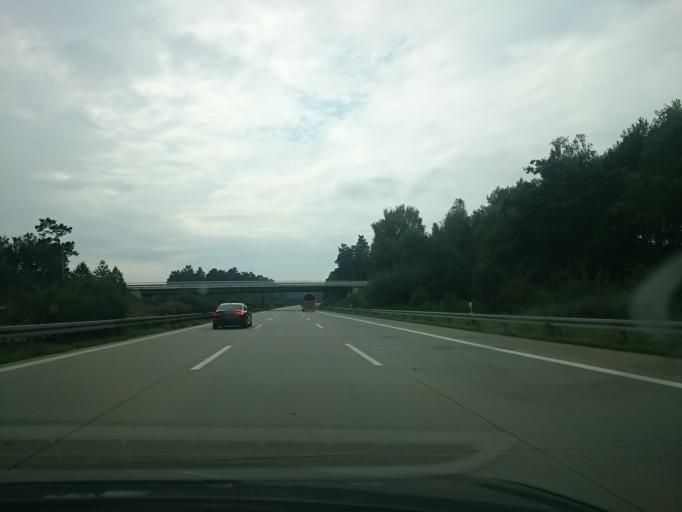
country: DE
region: Brandenburg
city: Niemegk
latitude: 52.0568
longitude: 12.6497
